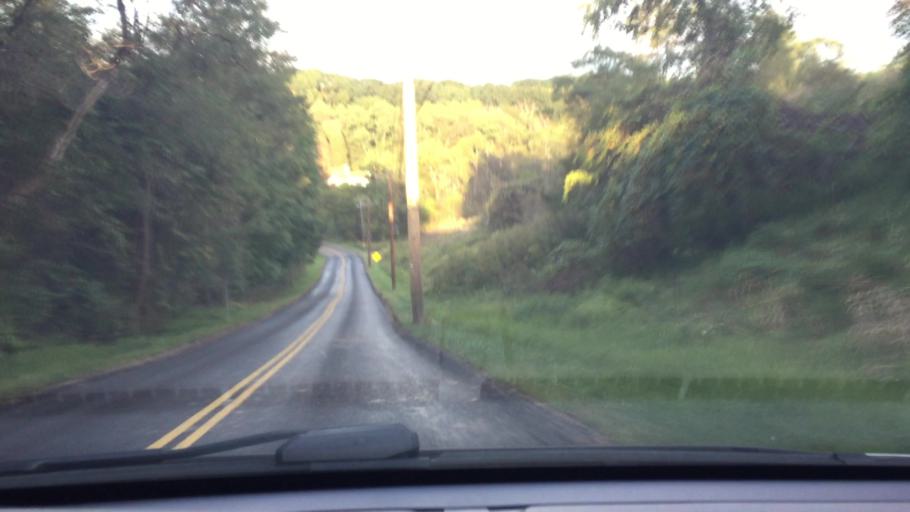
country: US
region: Pennsylvania
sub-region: Allegheny County
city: Plum
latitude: 40.4522
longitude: -79.7505
